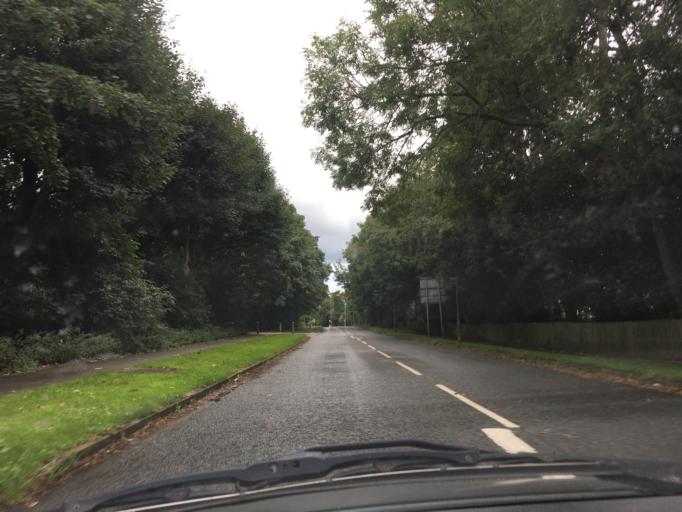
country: GB
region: England
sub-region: Leicestershire
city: Lutterworth
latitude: 52.4660
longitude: -1.2064
